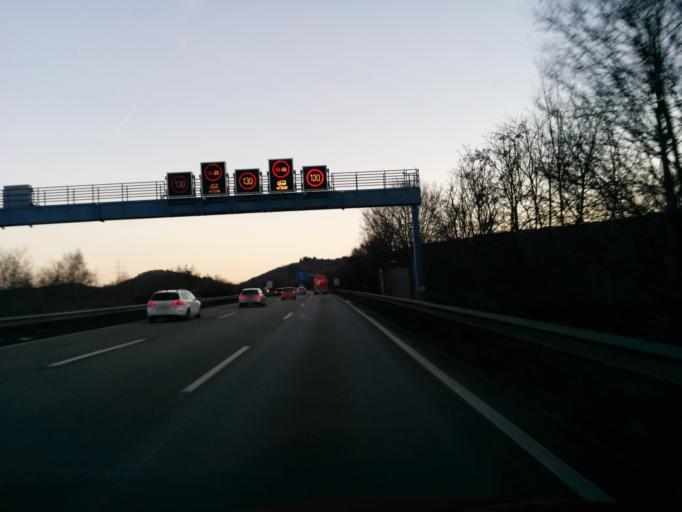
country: DE
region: Rheinland-Pfalz
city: Konigsfeld
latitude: 50.5381
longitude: 7.1697
